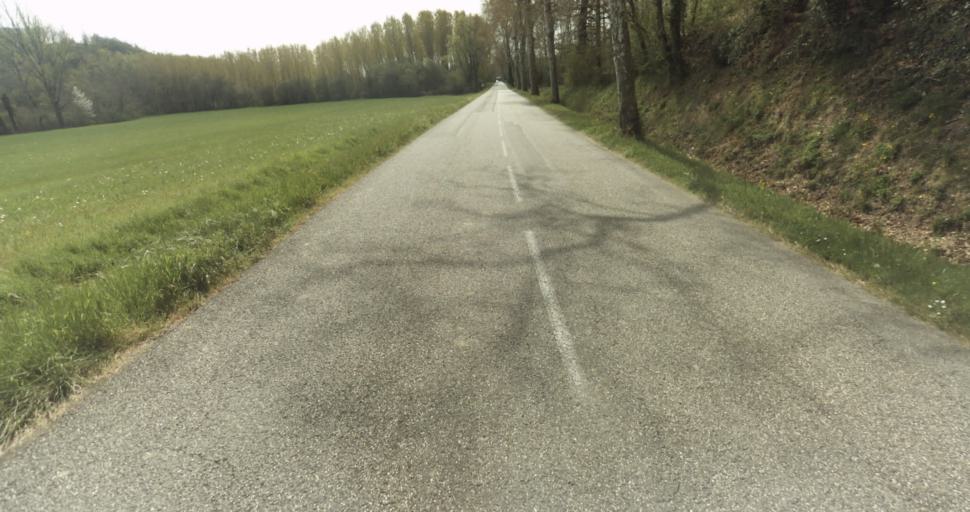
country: FR
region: Midi-Pyrenees
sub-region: Departement du Tarn-et-Garonne
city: Moissac
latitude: 44.1514
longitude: 1.1087
